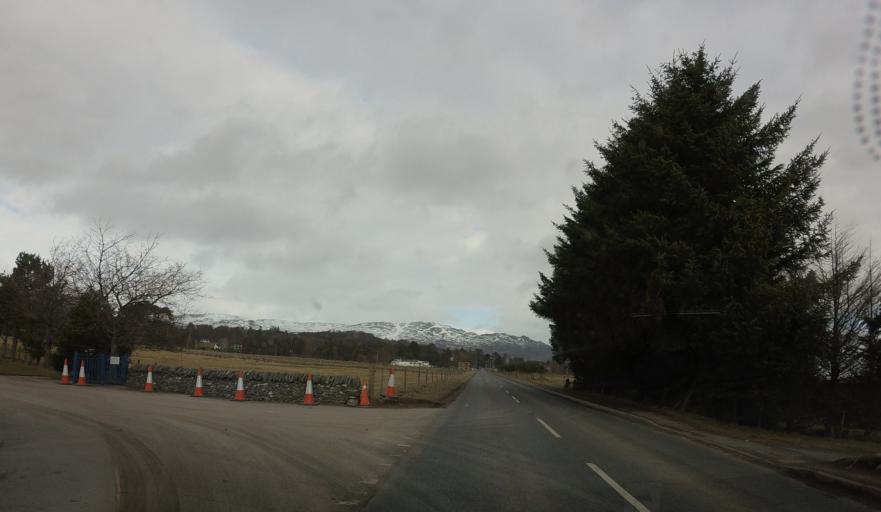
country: GB
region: Scotland
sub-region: Highland
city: Kingussie
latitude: 57.0572
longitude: -4.1302
